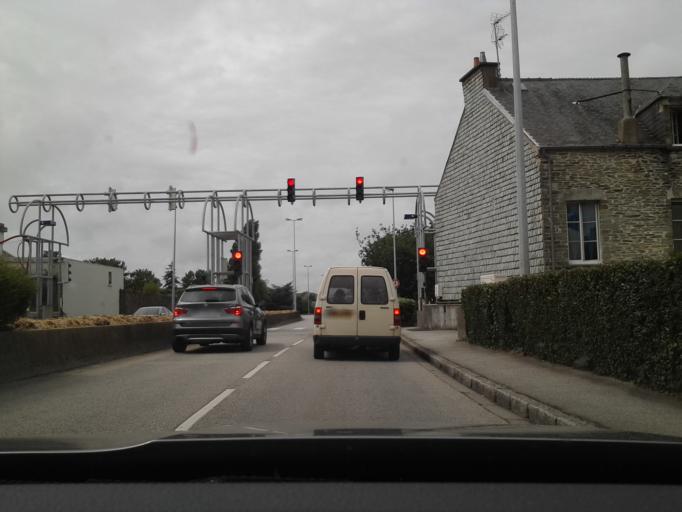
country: FR
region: Lower Normandy
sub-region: Departement de la Manche
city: Octeville
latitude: 49.6371
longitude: -1.6331
